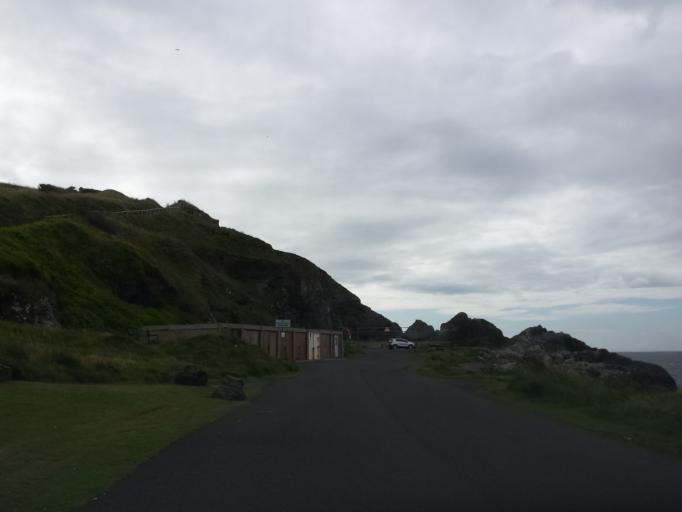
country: GB
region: Scotland
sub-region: Dumfries and Galloway
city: Stranraer
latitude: 54.8393
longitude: -5.1163
